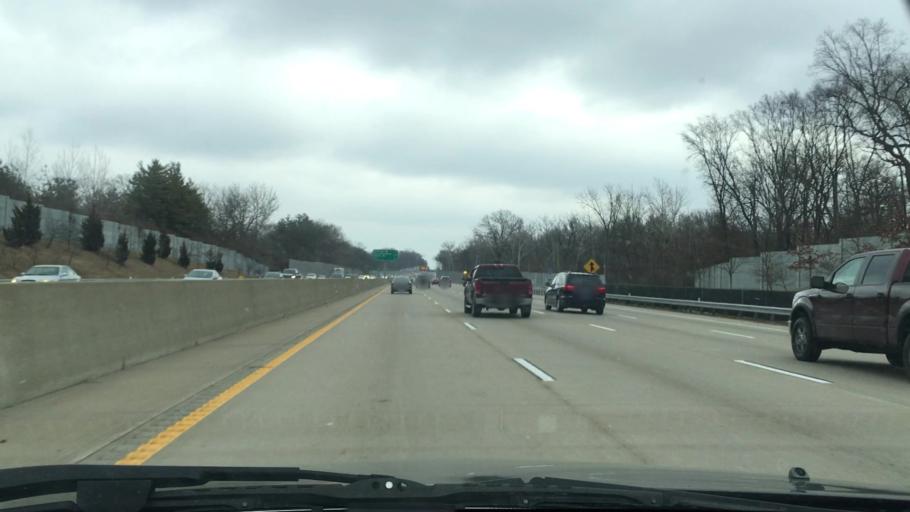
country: US
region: Missouri
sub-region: Saint Louis County
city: Ladue
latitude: 38.6316
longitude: -90.3806
